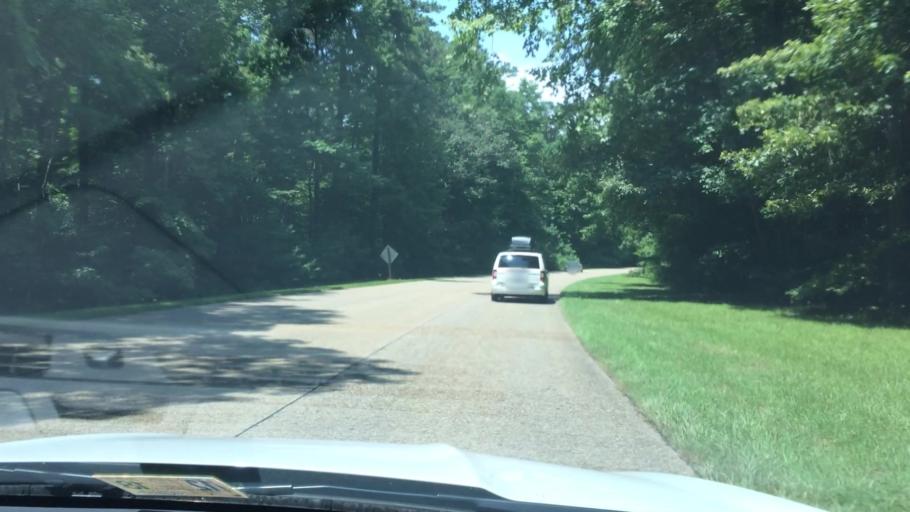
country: US
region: Virginia
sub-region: York County
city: Yorktown
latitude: 37.2302
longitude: -76.5199
